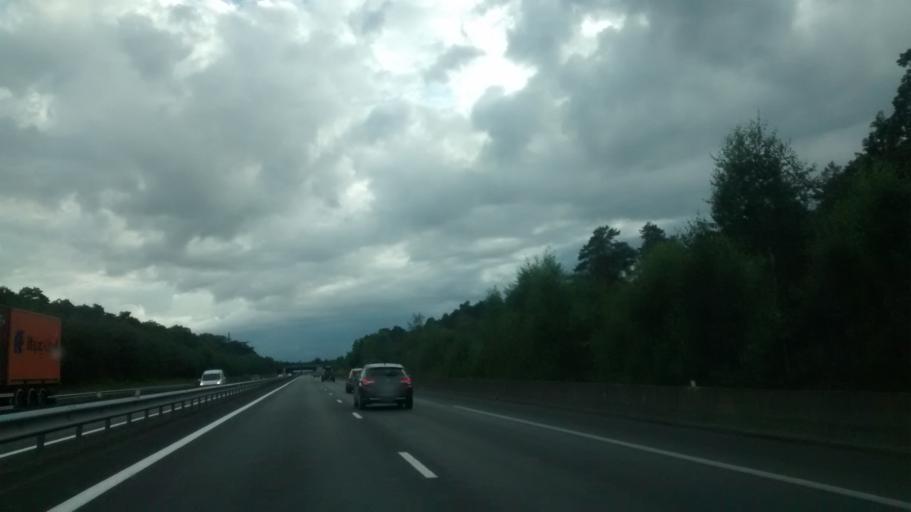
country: FR
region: Brittany
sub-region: Departement d'Ille-et-Vilaine
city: Liffre
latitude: 48.1941
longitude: -1.5390
